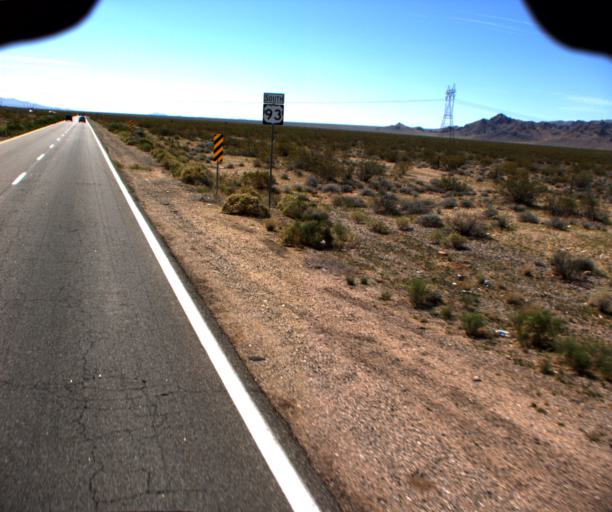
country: US
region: Arizona
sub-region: Mohave County
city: Dolan Springs
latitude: 35.6741
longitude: -114.4622
